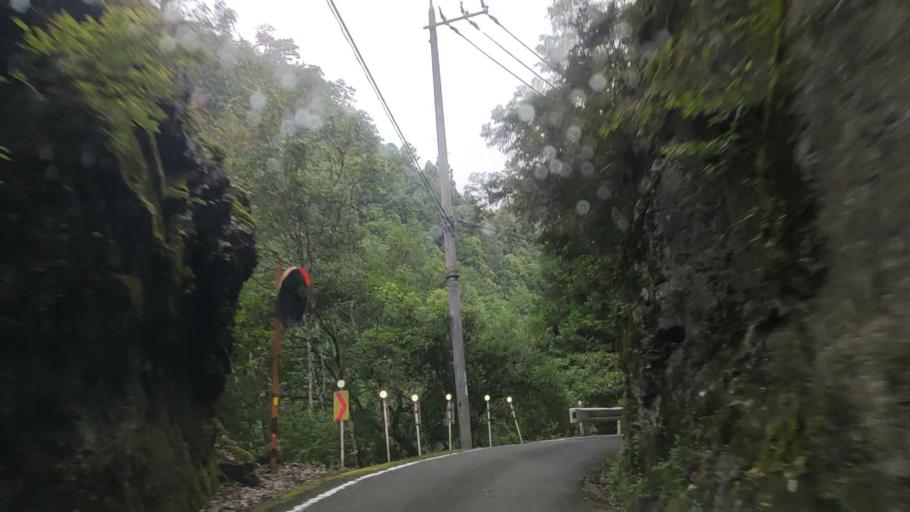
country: JP
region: Wakayama
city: Koya
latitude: 34.2601
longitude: 135.6489
